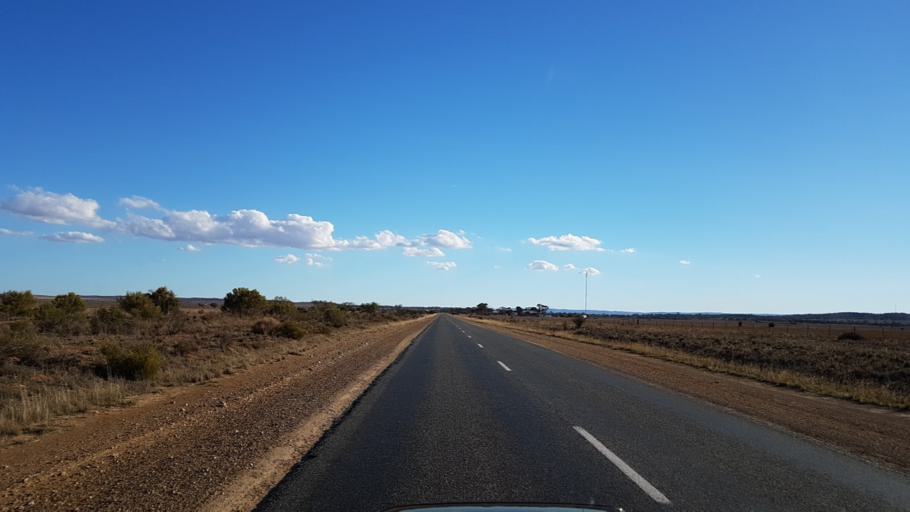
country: AU
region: South Australia
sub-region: Peterborough
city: Peterborough
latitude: -32.9653
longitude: 138.8779
